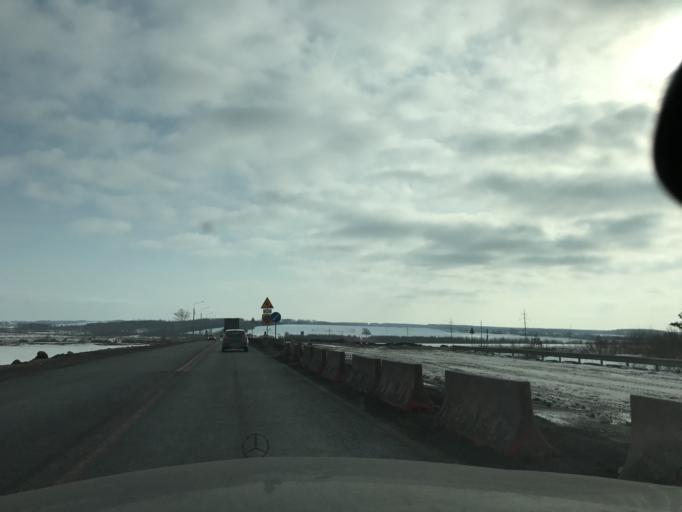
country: RU
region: Vladimir
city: Novovyazniki
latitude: 56.2176
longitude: 42.2201
